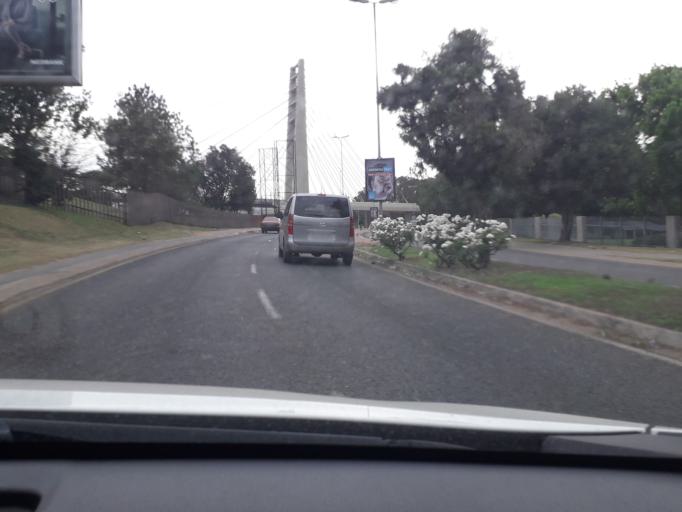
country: ZA
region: Gauteng
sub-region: City of Johannesburg Metropolitan Municipality
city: Modderfontein
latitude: -26.0955
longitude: 28.0828
